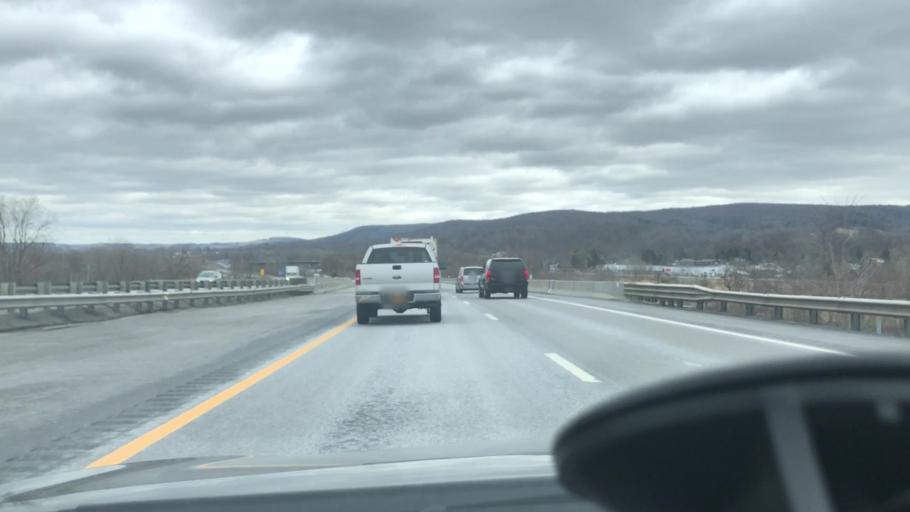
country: US
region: New York
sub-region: Herkimer County
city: Mohawk
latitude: 43.0179
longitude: -75.0111
